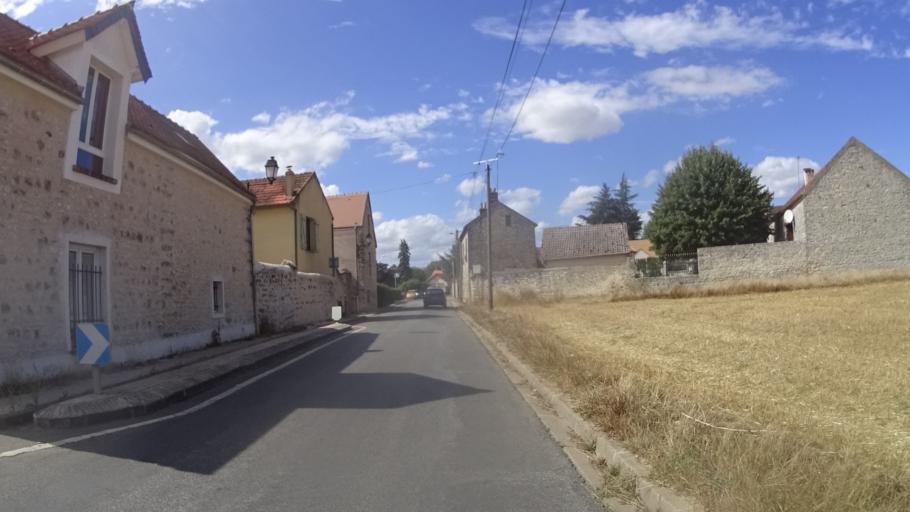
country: FR
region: Ile-de-France
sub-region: Departement de l'Essonne
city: Boutigny-sur-Essonne
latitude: 48.4256
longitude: 2.3863
